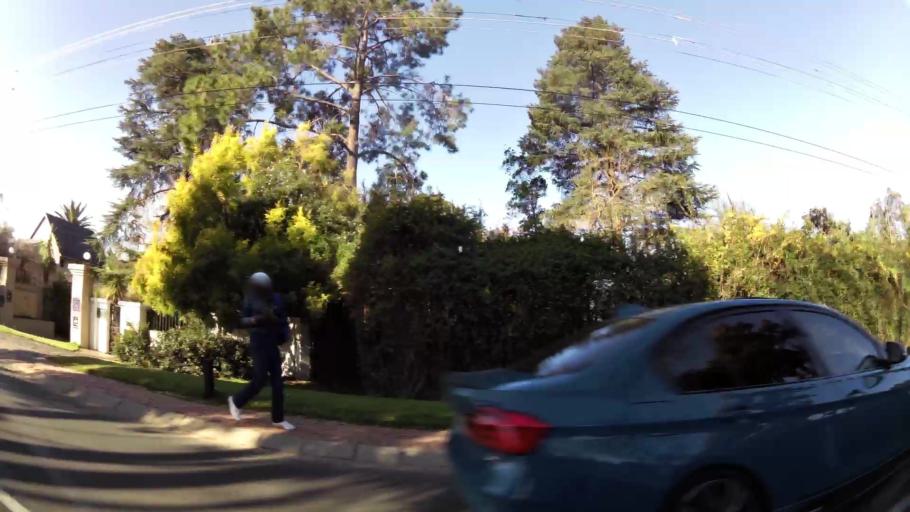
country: ZA
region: Gauteng
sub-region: City of Johannesburg Metropolitan Municipality
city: Johannesburg
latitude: -26.1122
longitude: 28.0705
